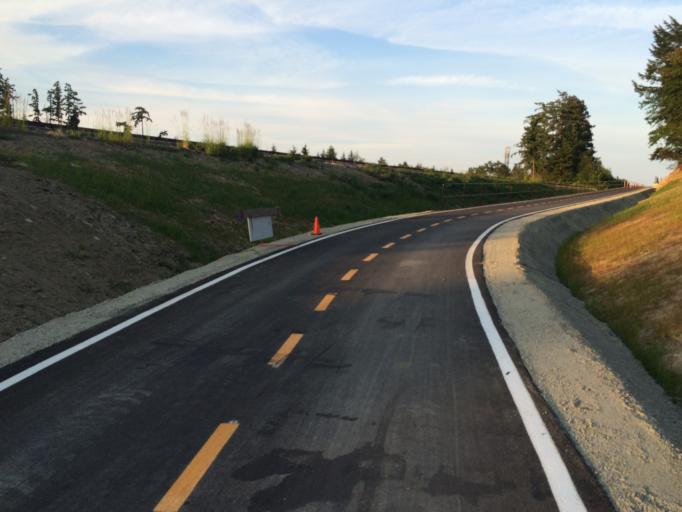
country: CA
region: British Columbia
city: Colwood
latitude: 48.4605
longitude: -123.4511
